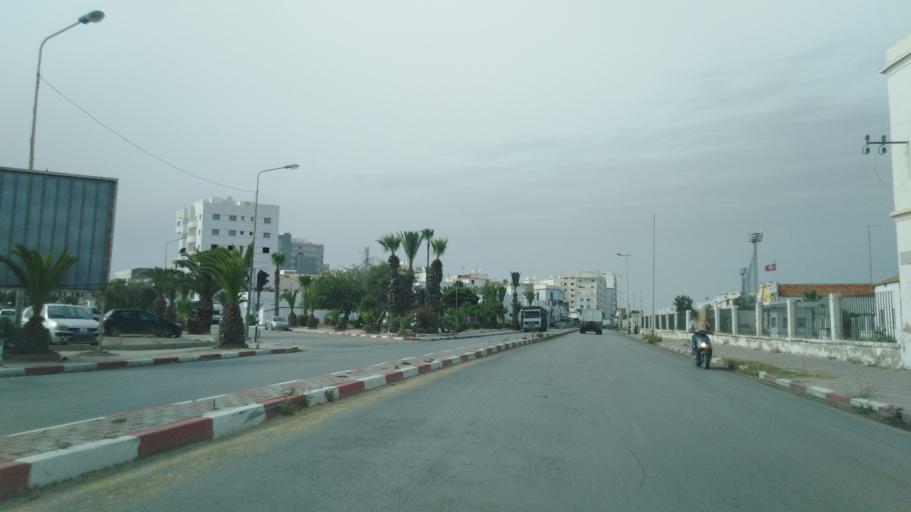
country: TN
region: Safaqis
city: Sfax
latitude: 34.7399
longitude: 10.7636
